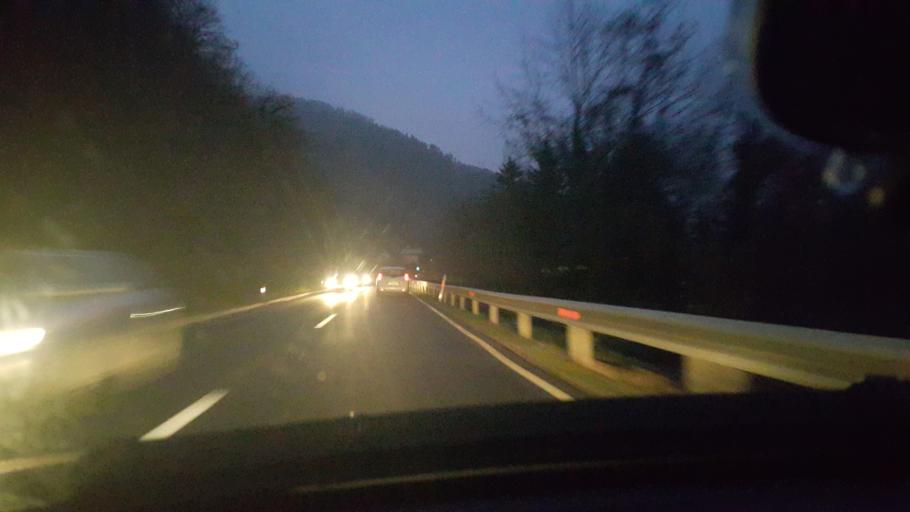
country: SI
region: Muta
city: Muta
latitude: 46.6062
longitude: 15.0976
